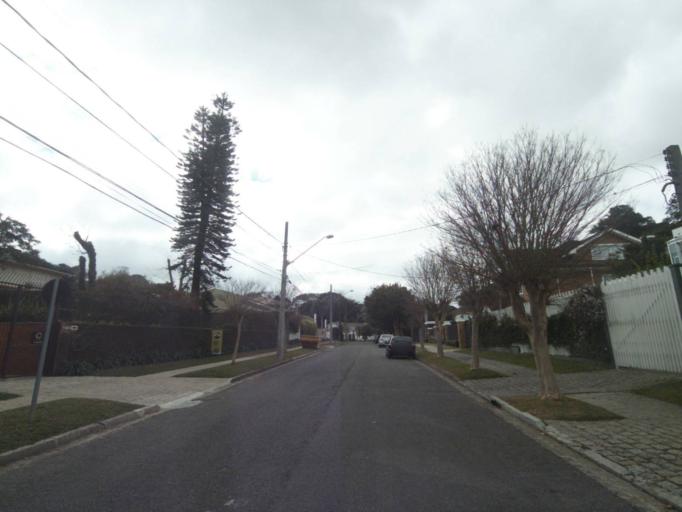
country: BR
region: Parana
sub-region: Curitiba
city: Curitiba
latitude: -25.4470
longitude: -49.3019
